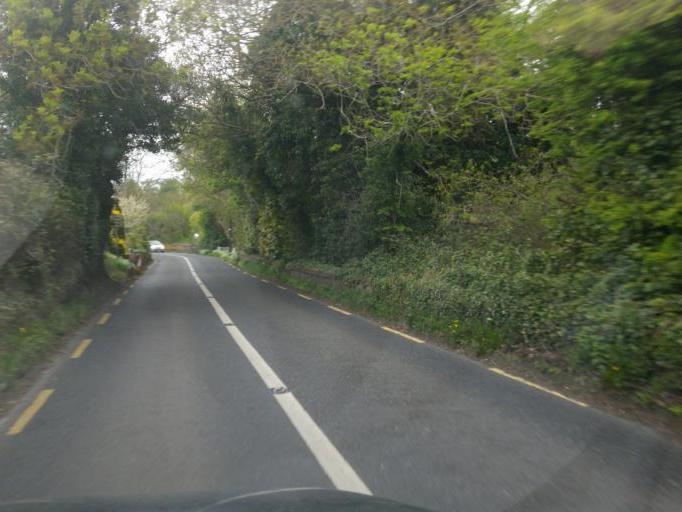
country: IE
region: Leinster
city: Castleknock
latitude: 53.3827
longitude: -6.3534
